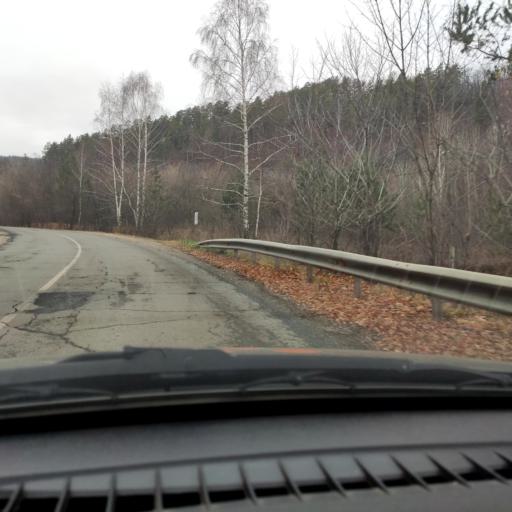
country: RU
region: Samara
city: Zhigulevsk
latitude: 53.4281
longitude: 49.6627
